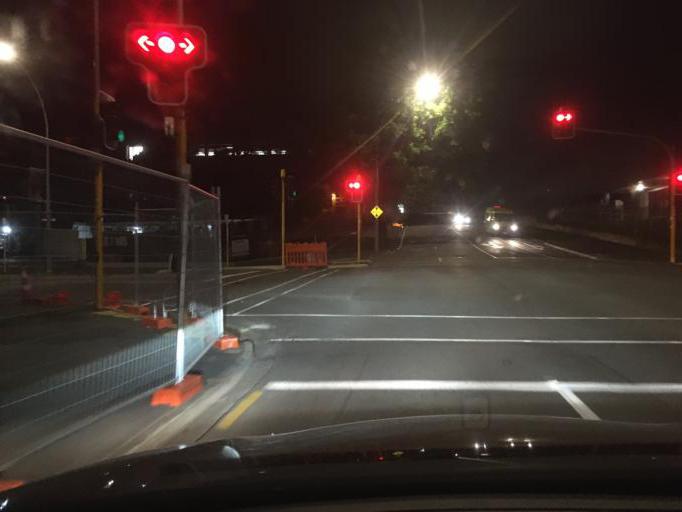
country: NZ
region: Waikato
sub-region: Hamilton City
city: Hamilton
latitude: -37.7883
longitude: 175.2772
